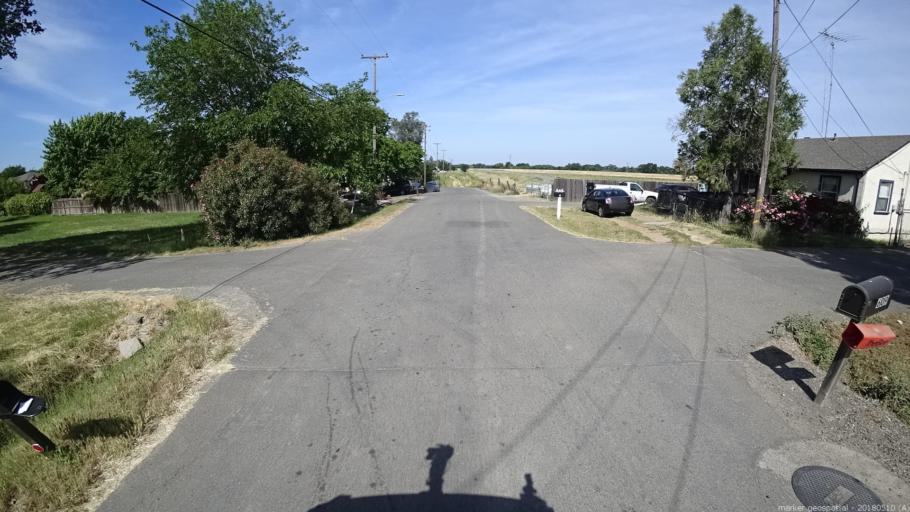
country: US
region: California
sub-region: Sacramento County
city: Rio Linda
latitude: 38.6621
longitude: -121.4520
